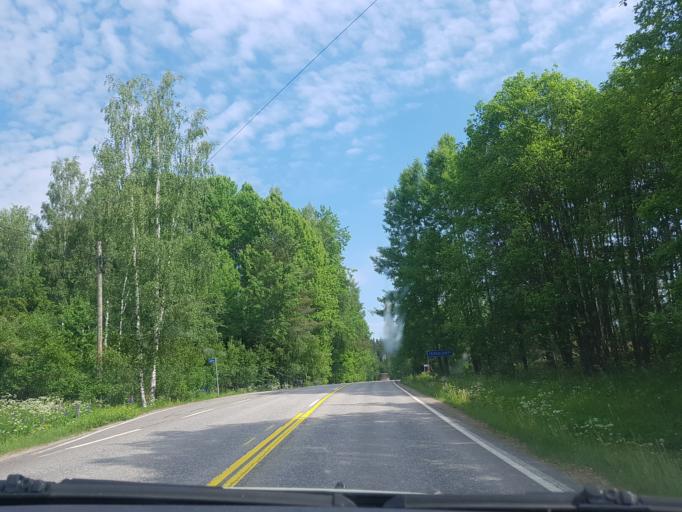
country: FI
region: Uusimaa
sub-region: Helsinki
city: Vihti
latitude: 60.2978
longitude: 24.3990
